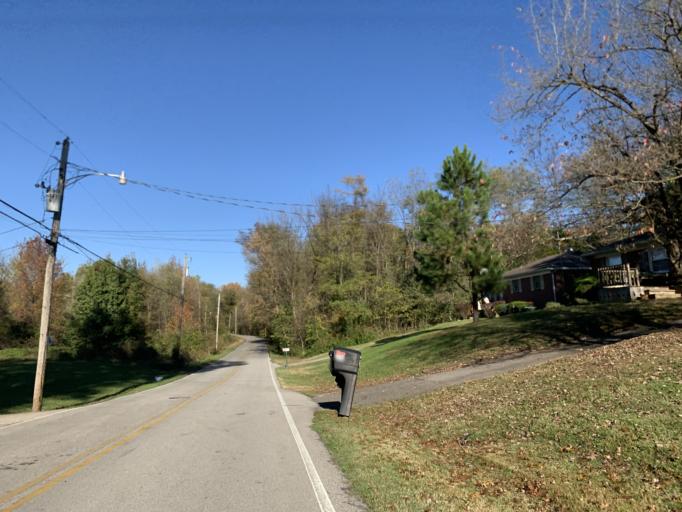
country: US
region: Kentucky
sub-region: Jefferson County
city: Pleasure Ridge Park
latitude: 38.1477
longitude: -85.8803
